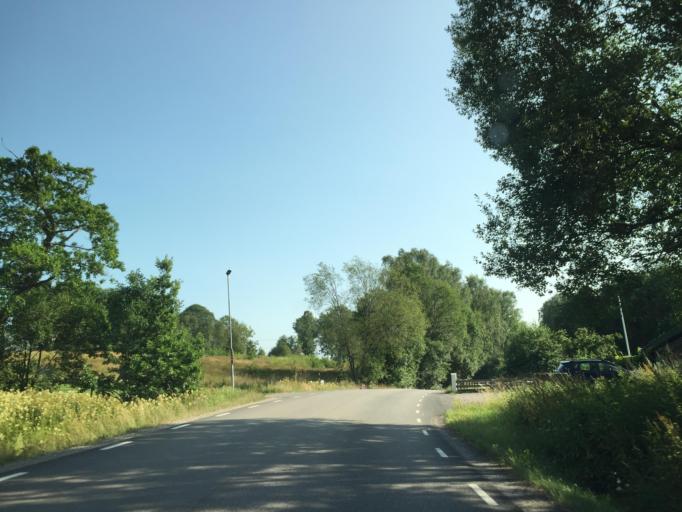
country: SE
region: Vaestra Goetaland
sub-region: Trollhattan
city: Trollhattan
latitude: 58.2835
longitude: 12.2493
